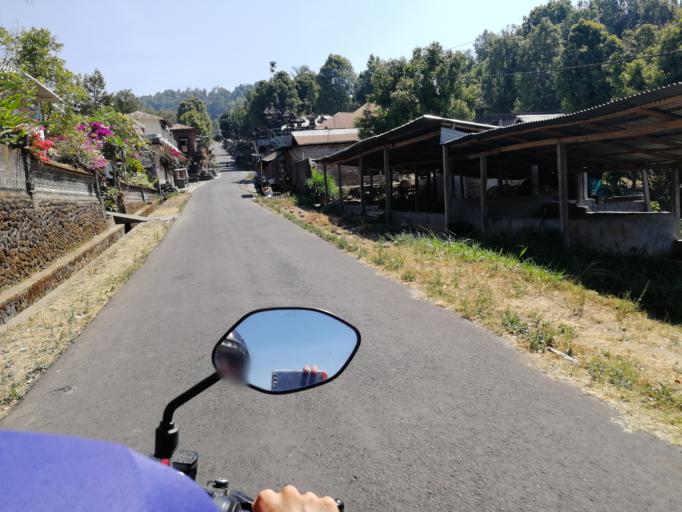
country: ID
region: Bali
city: Banjar Kedisan
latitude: -8.1648
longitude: 115.3038
